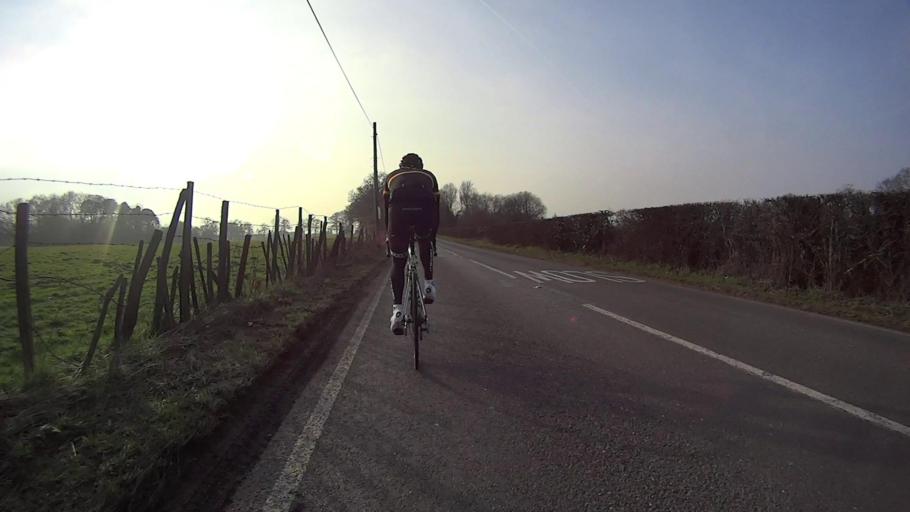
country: GB
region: England
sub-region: West Sussex
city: Copthorne
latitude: 51.1151
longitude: -0.1261
